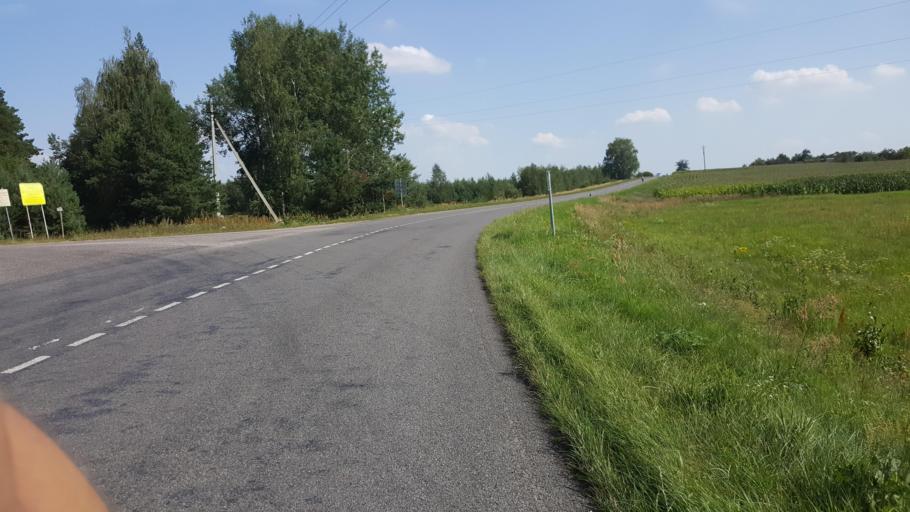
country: BY
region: Brest
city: Kamyanyuki
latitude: 52.5036
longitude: 23.6610
